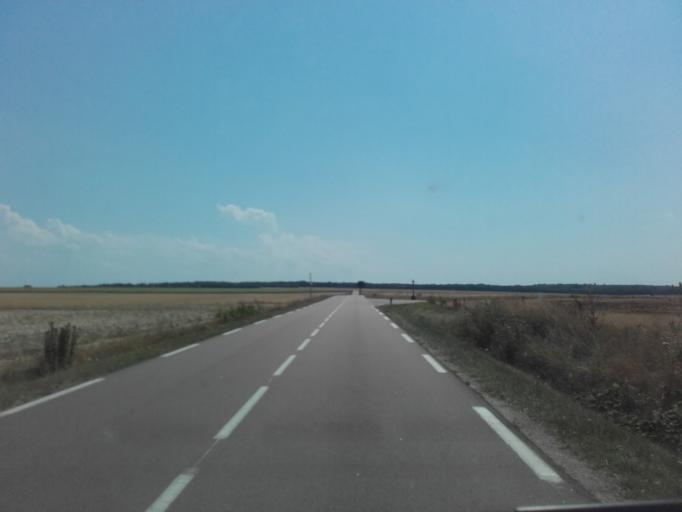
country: FR
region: Bourgogne
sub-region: Departement de l'Yonne
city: Joux-la-Ville
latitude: 47.7235
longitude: 3.8533
